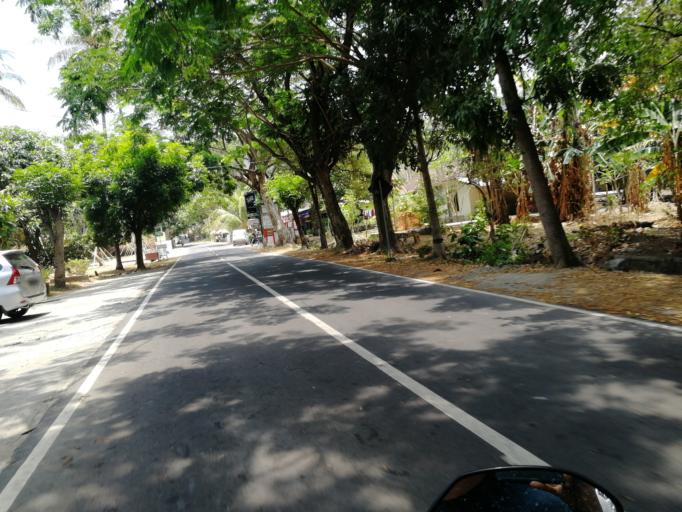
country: ID
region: West Nusa Tenggara
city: Karangsubagan
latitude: -8.4581
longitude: 116.0387
